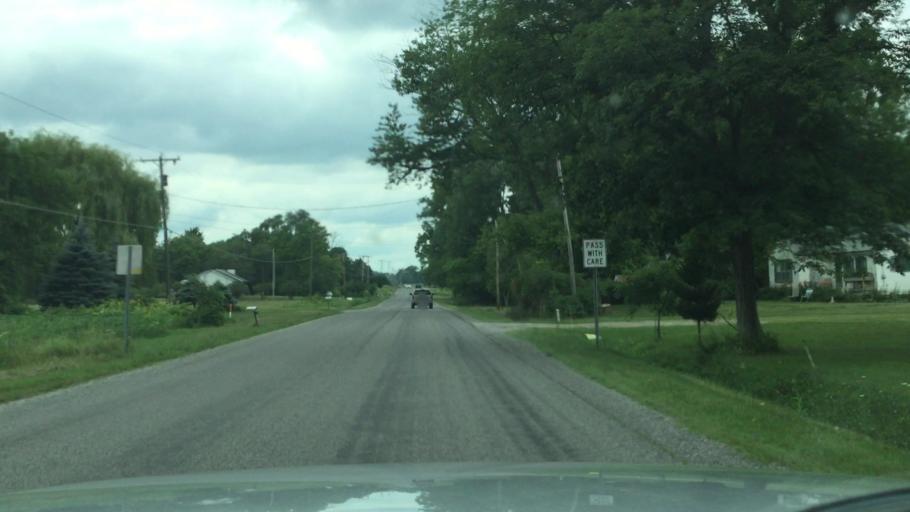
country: US
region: Michigan
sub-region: Saginaw County
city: Birch Run
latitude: 43.2507
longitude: -83.8273
